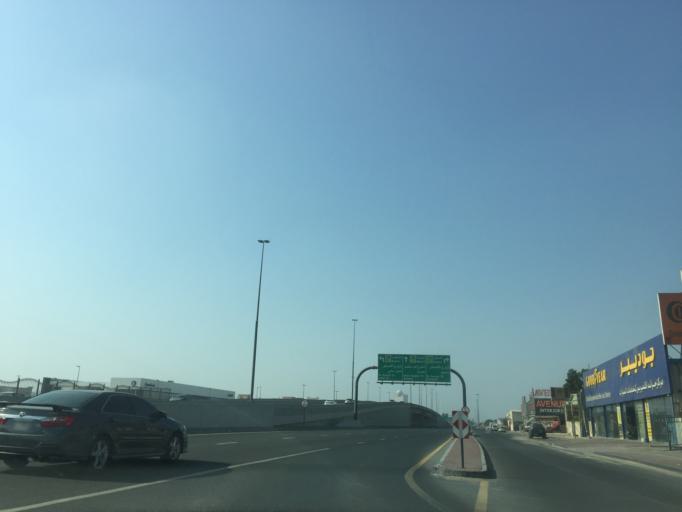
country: AE
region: Dubai
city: Dubai
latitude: 25.1095
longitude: 55.2226
